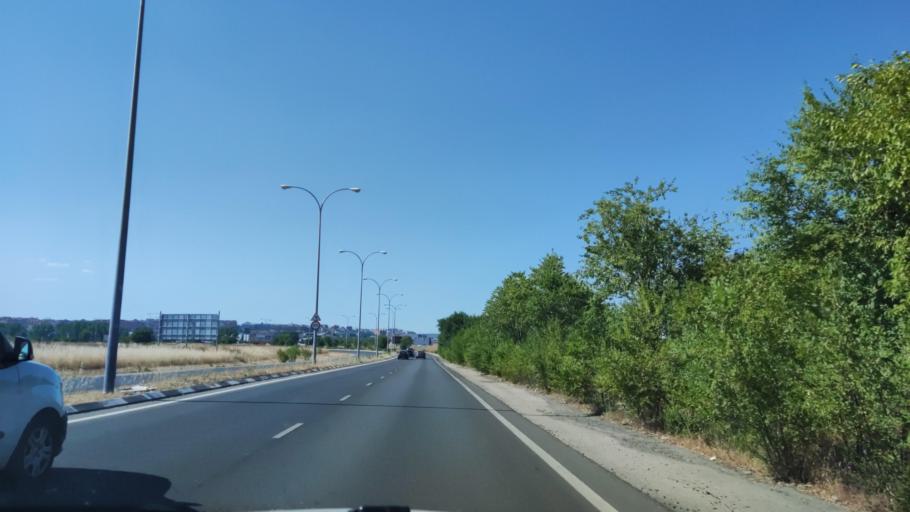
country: ES
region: Madrid
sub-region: Provincia de Madrid
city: Leganes
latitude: 40.3446
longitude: -3.7388
